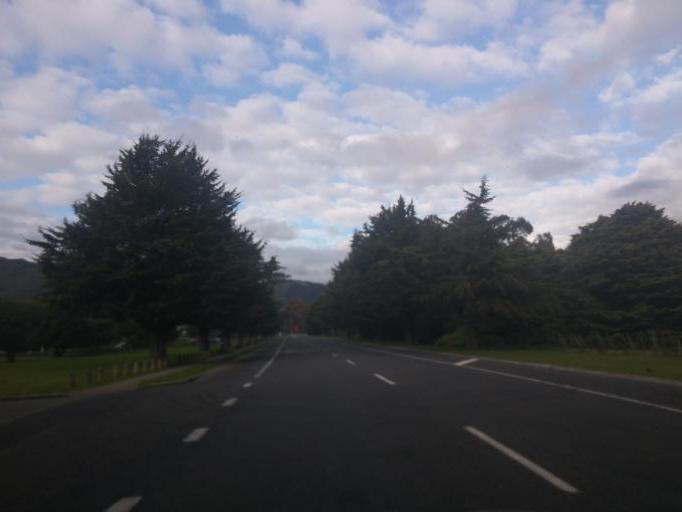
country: NZ
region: Wellington
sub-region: Kapiti Coast District
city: Paraparaumu
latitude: -40.8745
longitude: 175.0485
